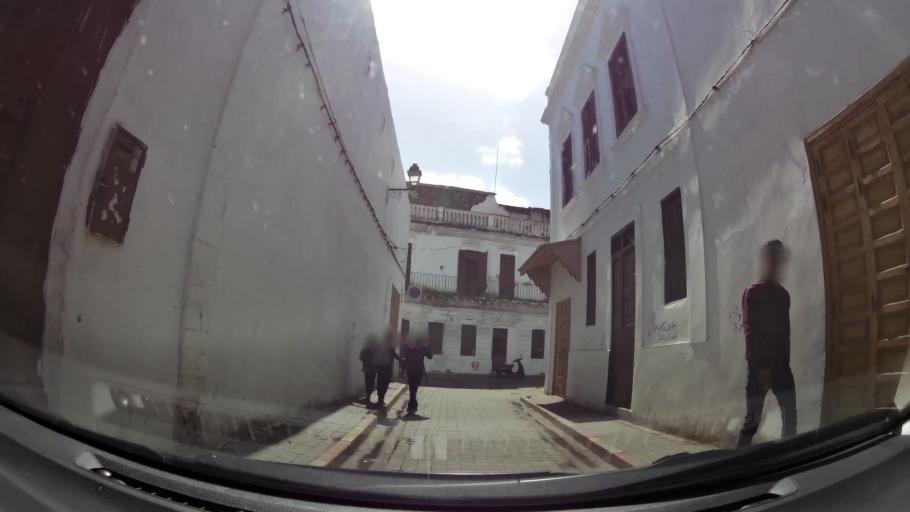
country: MA
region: Grand Casablanca
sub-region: Casablanca
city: Casablanca
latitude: 33.6008
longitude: -7.6180
